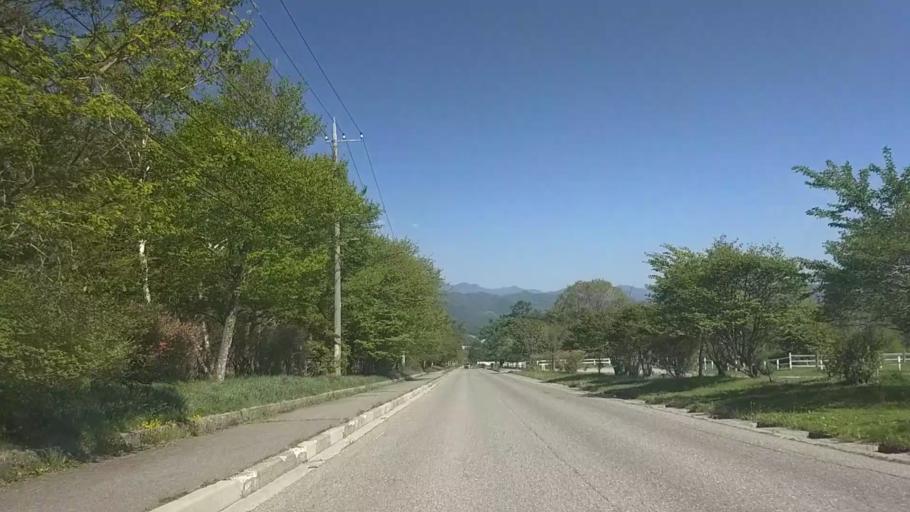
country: JP
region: Yamanashi
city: Nirasaki
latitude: 35.9245
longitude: 138.4223
